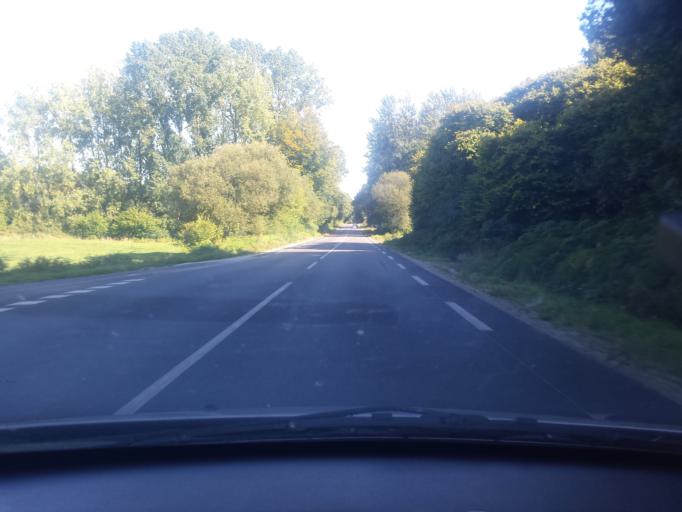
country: FR
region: Brittany
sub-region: Departement du Morbihan
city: Malguenac
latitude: 48.0998
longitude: -3.0613
